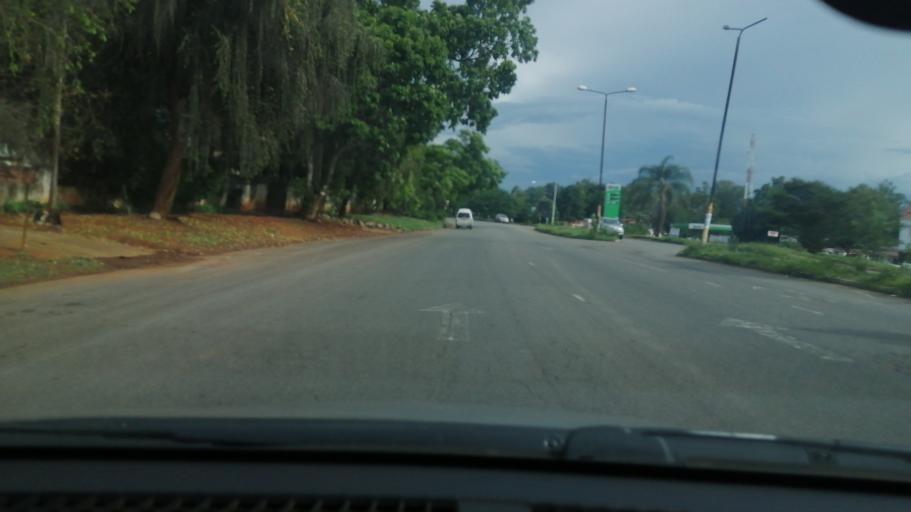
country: ZW
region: Harare
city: Harare
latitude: -17.7802
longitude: 31.0286
